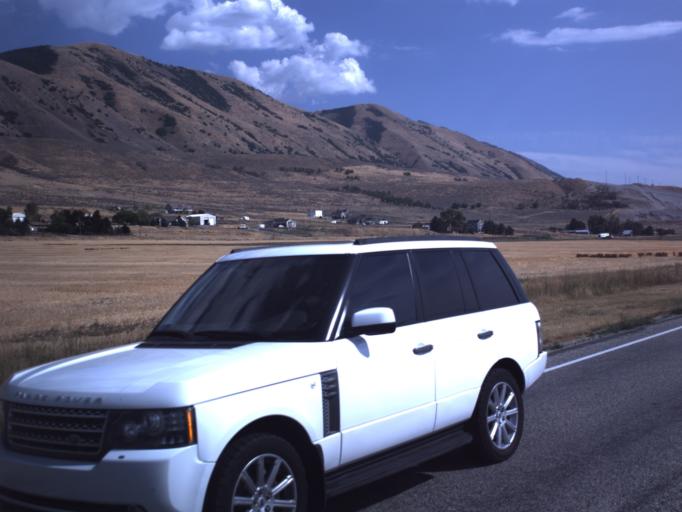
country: US
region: Utah
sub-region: Box Elder County
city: Garland
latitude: 41.7625
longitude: -112.0976
